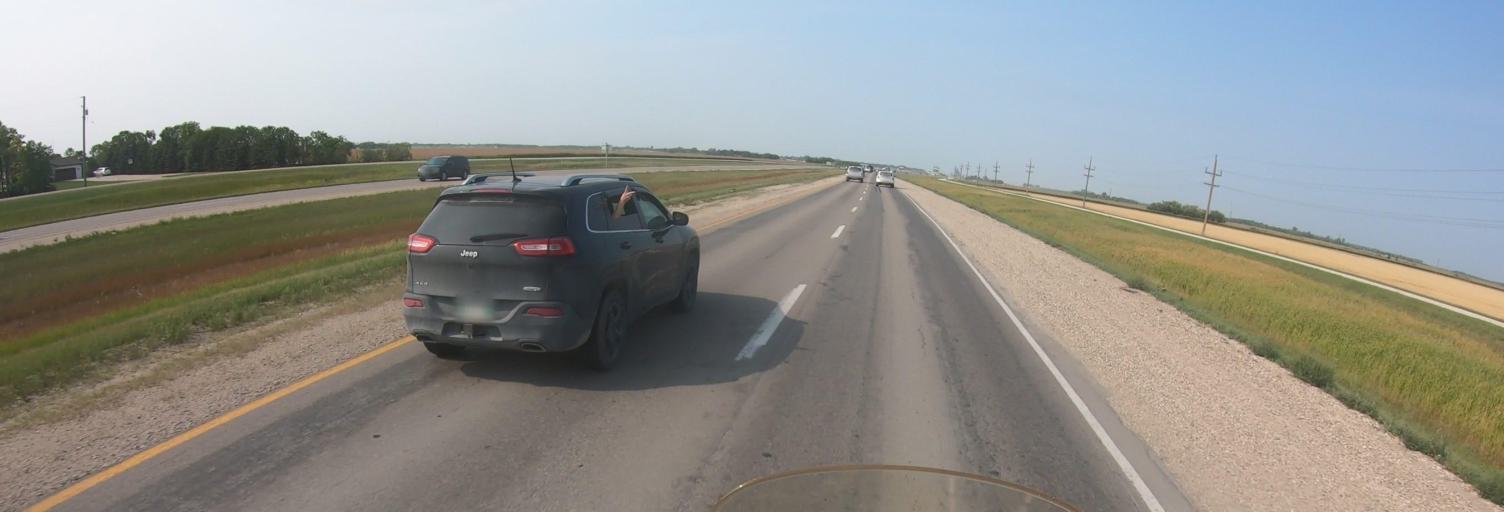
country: CA
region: Manitoba
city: Steinbach
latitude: 49.5782
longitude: -96.6868
